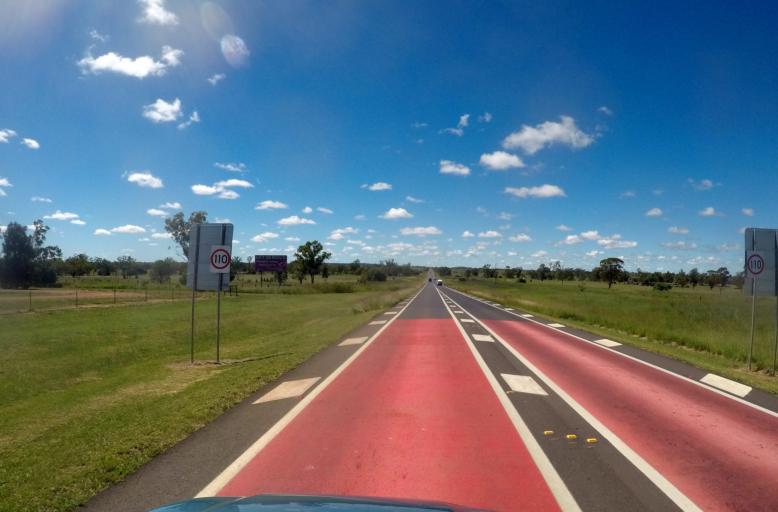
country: AU
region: Queensland
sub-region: Western Downs
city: Westcourt
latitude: -26.6446
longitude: 149.7690
